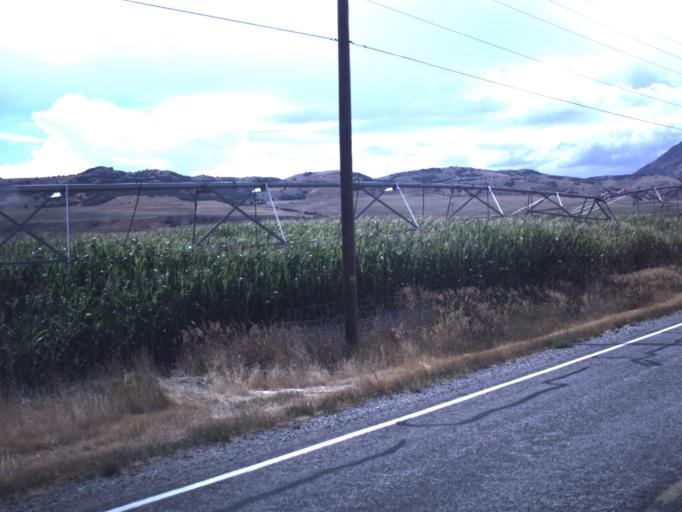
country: US
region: Utah
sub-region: Cache County
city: Benson
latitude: 41.8698
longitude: -112.0128
